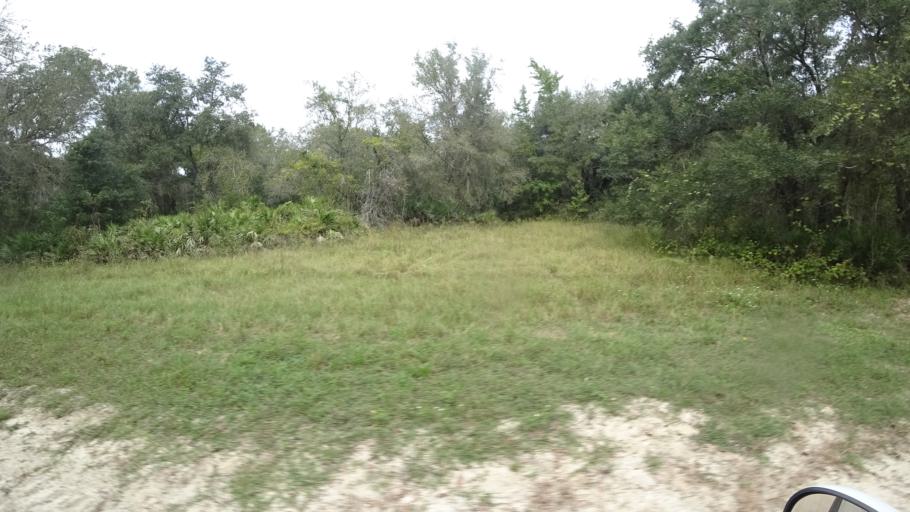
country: US
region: Florida
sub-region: Hillsborough County
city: Wimauma
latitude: 27.6296
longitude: -82.2784
